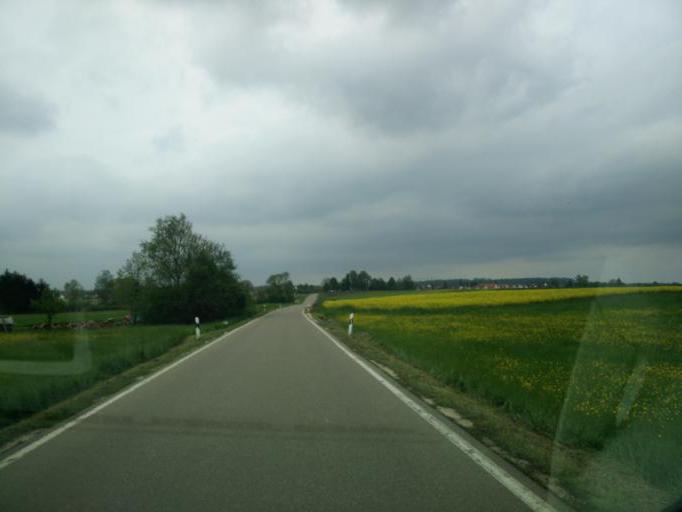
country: DE
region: Baden-Wuerttemberg
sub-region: Tuebingen Region
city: Gomaringen
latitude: 48.4779
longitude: 9.1127
